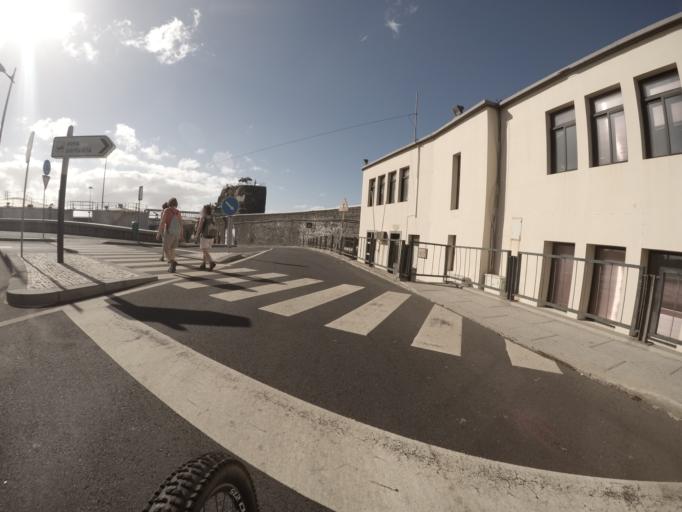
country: PT
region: Madeira
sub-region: Funchal
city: Funchal
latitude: 32.6421
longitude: -16.9180
